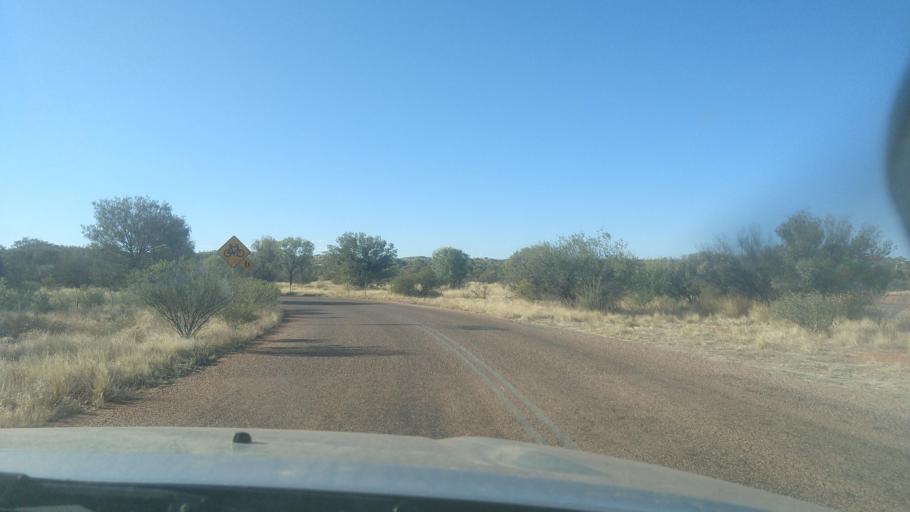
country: AU
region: Northern Territory
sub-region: Alice Springs
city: Alice Springs
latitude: -23.7040
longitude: 133.8334
